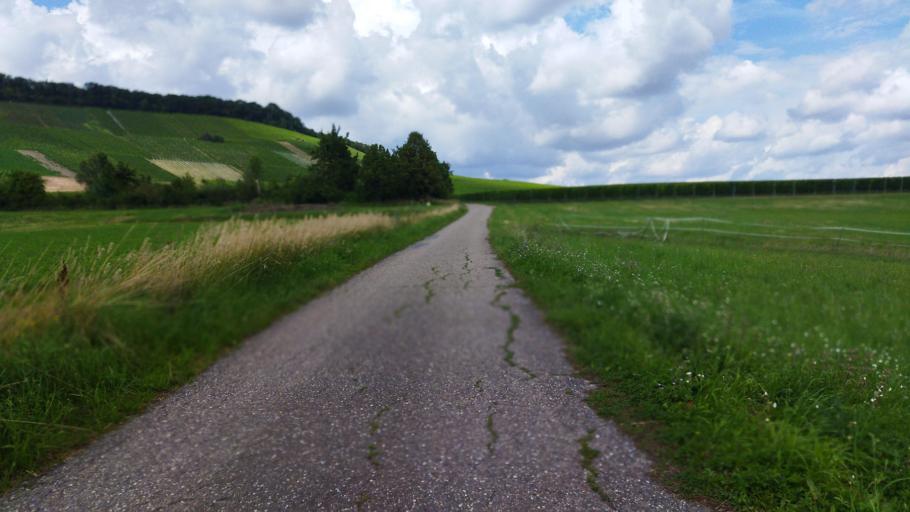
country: DE
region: Baden-Wuerttemberg
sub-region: Regierungsbezirk Stuttgart
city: Brackenheim
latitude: 49.0956
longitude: 9.0748
